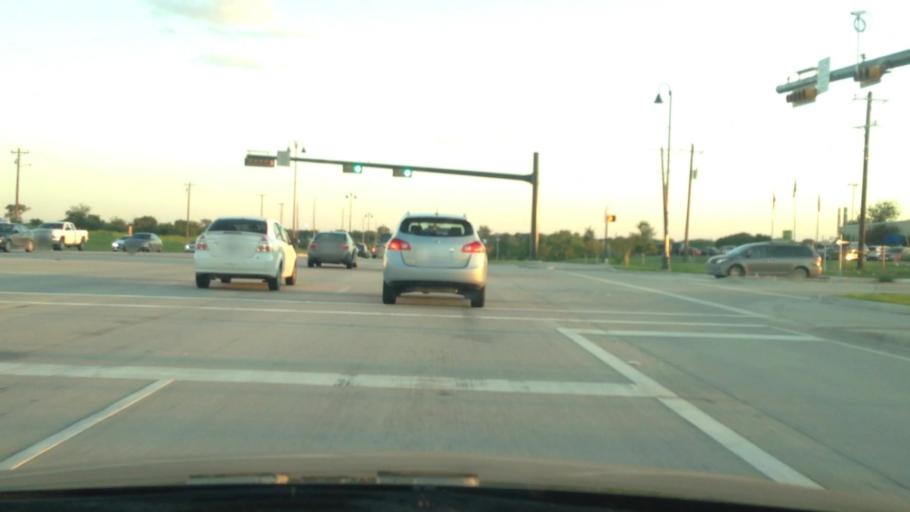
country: US
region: Texas
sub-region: Denton County
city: The Colony
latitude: 33.1145
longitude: -96.8921
